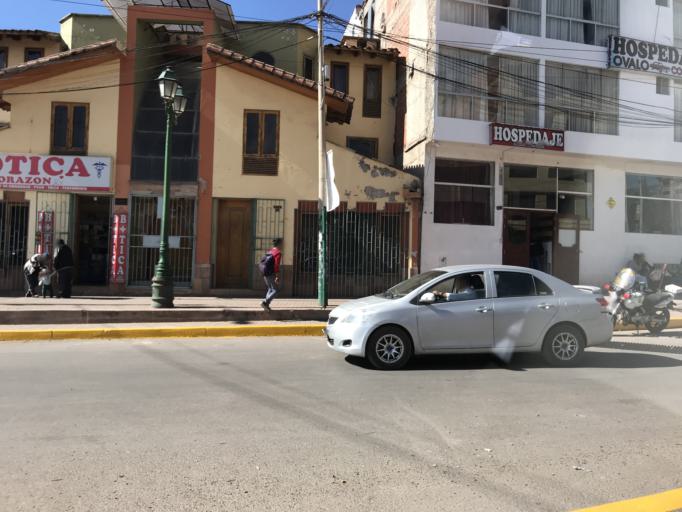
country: PE
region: Cusco
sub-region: Provincia de Cusco
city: Cusco
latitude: -13.5318
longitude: -71.9690
